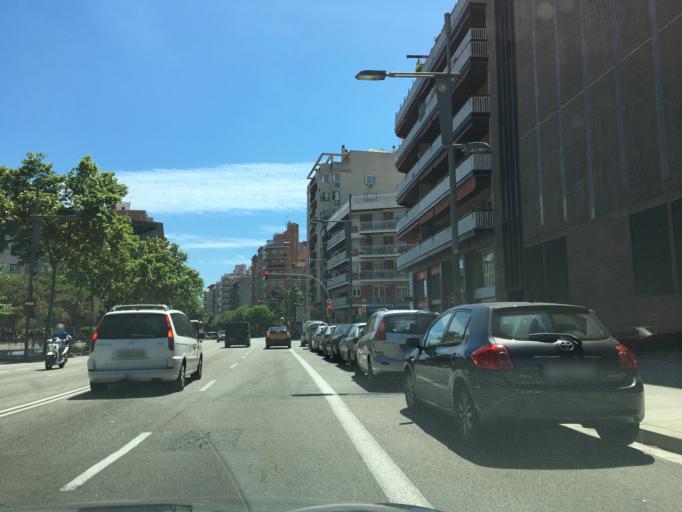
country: ES
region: Catalonia
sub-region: Provincia de Barcelona
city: Horta-Guinardo
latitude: 41.4170
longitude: 2.1804
